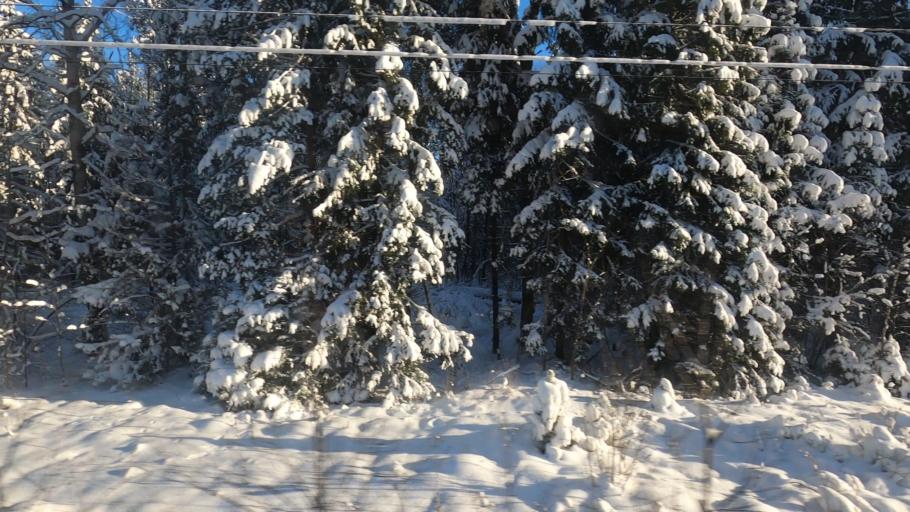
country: RU
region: Moskovskaya
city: Verbilki
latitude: 56.5130
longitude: 37.5557
